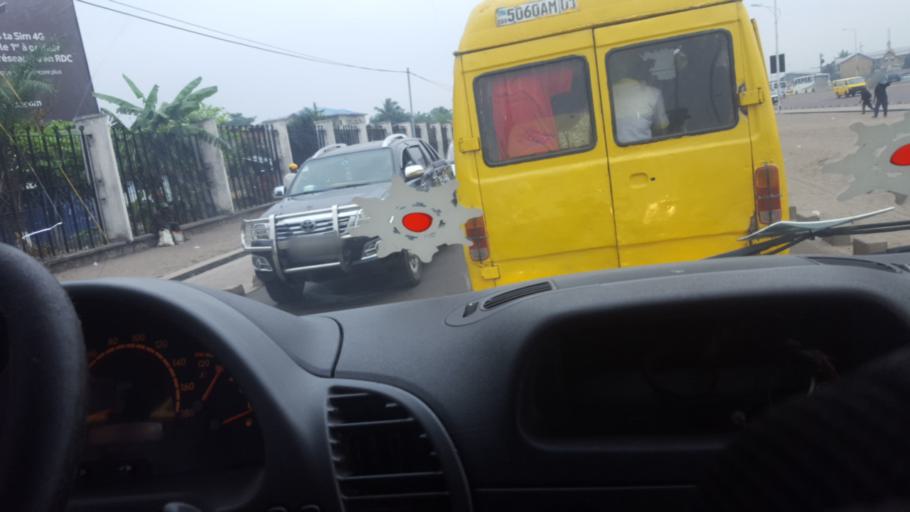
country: CD
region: Kinshasa
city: Kinshasa
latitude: -4.3681
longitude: 15.3426
